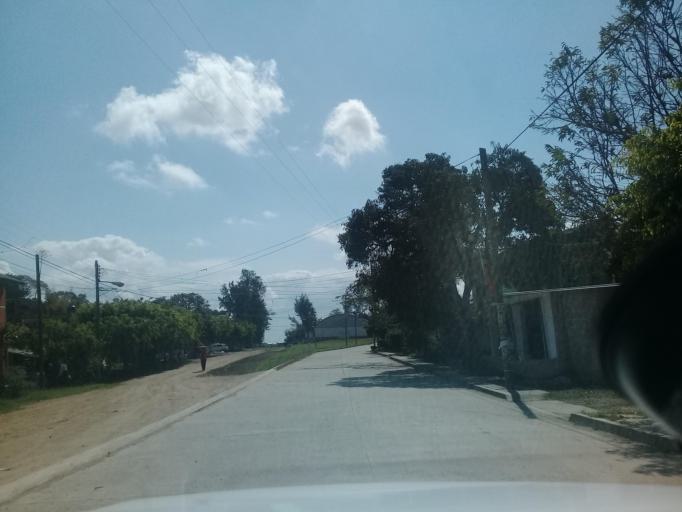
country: MX
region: Veracruz
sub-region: Coatepec
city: Bella Esperanza
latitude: 19.4382
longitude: -96.8685
